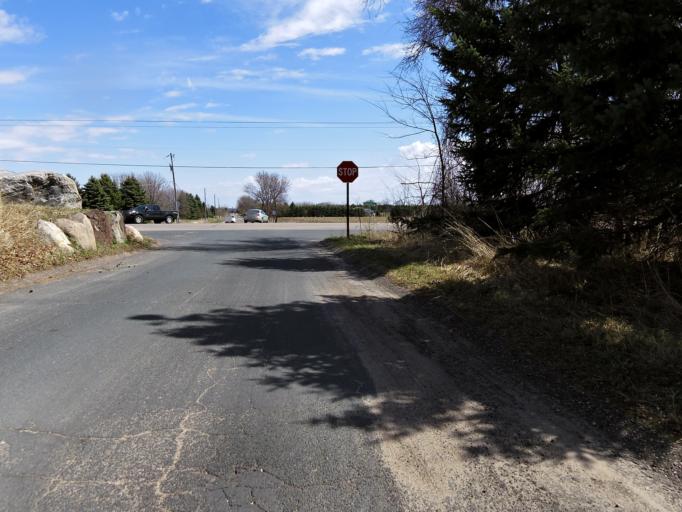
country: US
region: Minnesota
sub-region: Washington County
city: Lakeland
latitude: 44.9802
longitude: -92.7917
